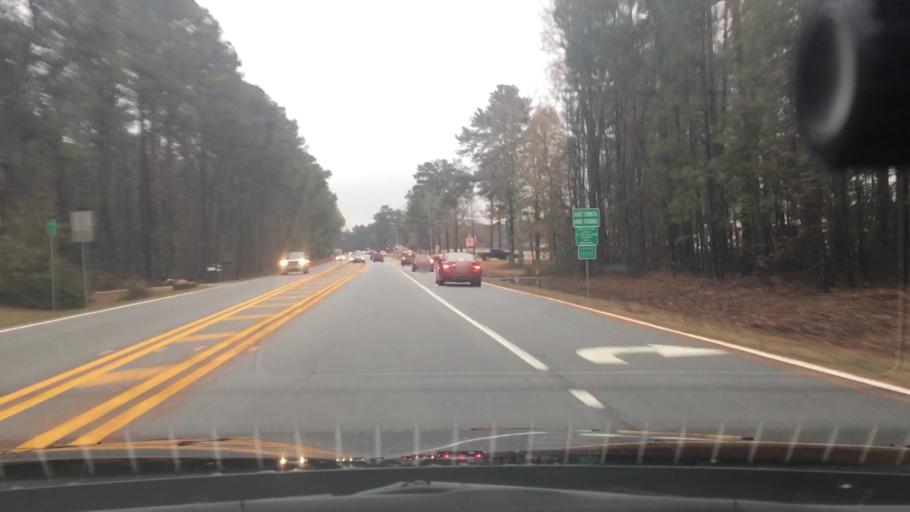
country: US
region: Georgia
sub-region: Fayette County
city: Peachtree City
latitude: 33.3505
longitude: -84.6573
